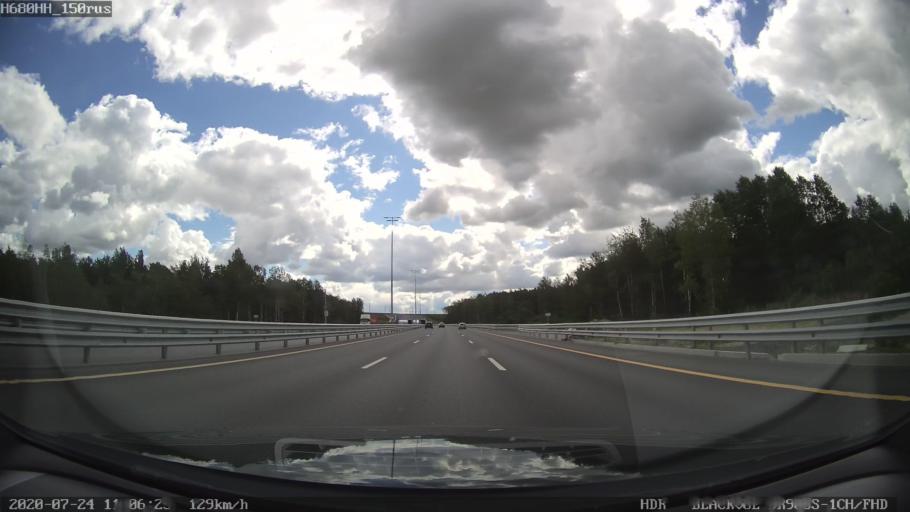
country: RU
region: St.-Petersburg
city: Shushary
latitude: 59.7632
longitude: 30.3749
